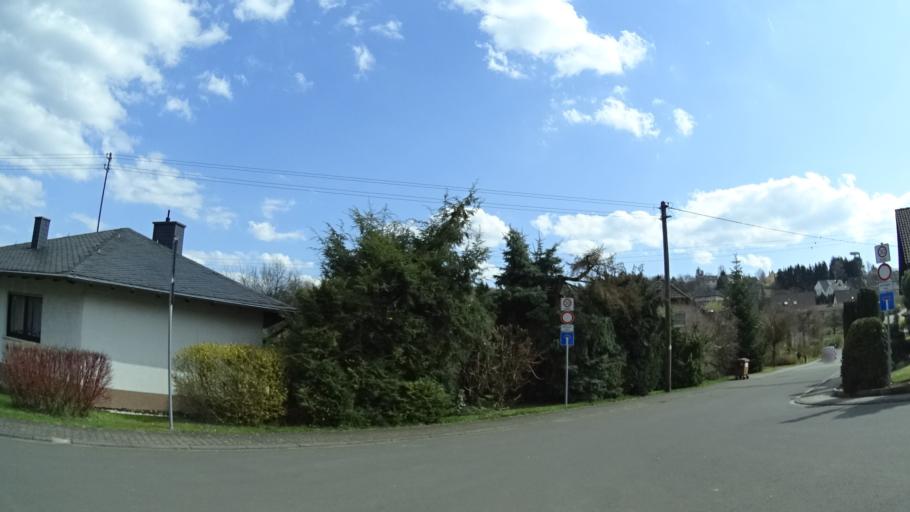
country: DE
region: Rheinland-Pfalz
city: Kirschweiler
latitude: 49.7419
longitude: 7.2550
